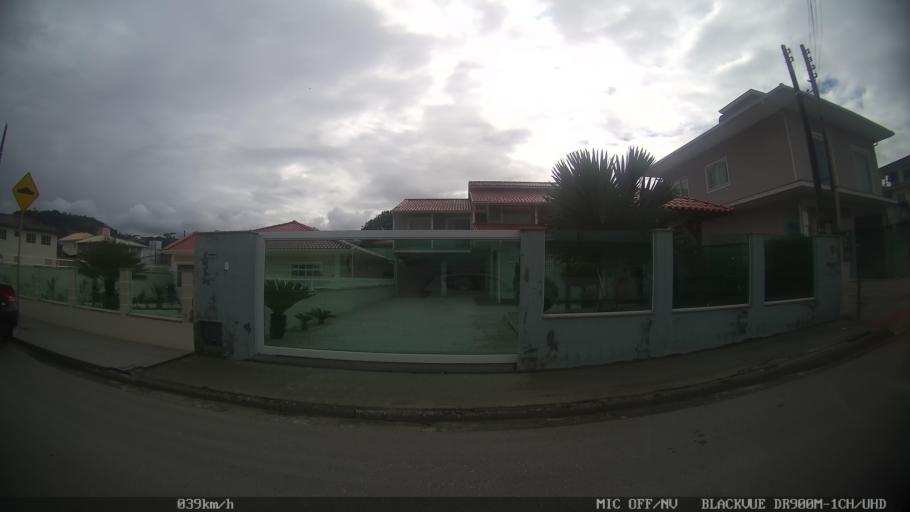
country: BR
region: Santa Catarina
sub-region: Sao Jose
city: Campinas
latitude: -27.5489
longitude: -48.6310
